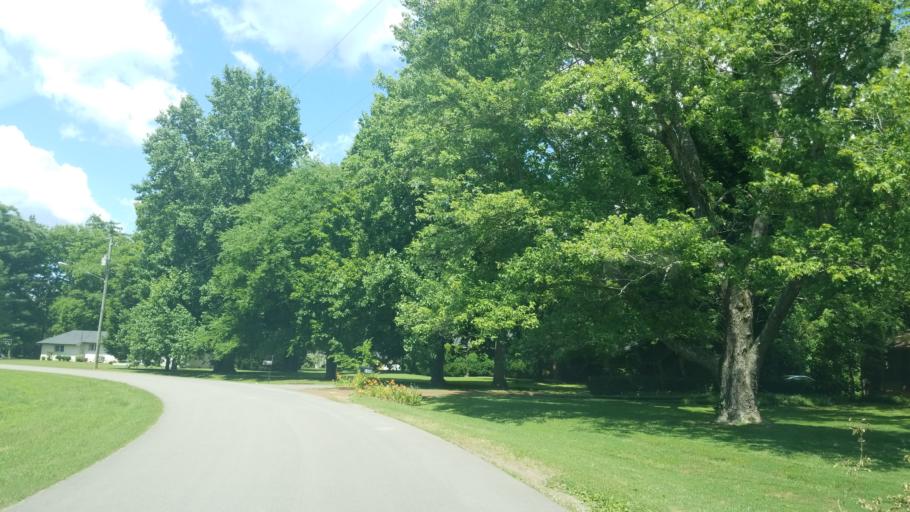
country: US
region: Tennessee
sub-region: Williamson County
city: Brentwood
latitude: 36.0281
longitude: -86.7993
